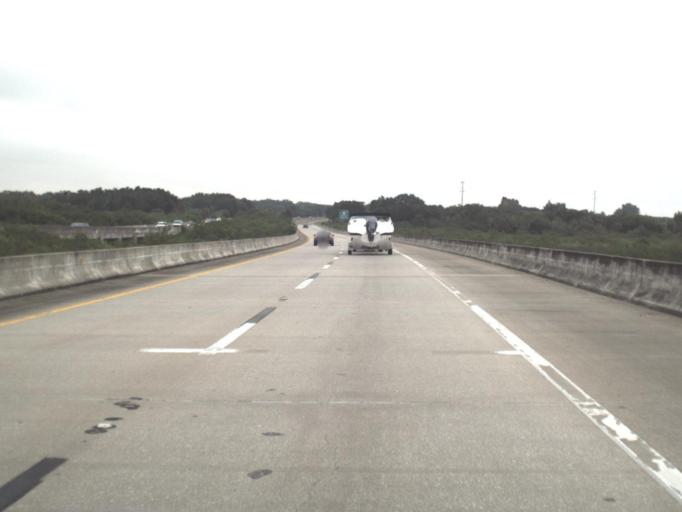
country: US
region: Florida
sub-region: Manatee County
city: Memphis
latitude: 27.5812
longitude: -82.5645
